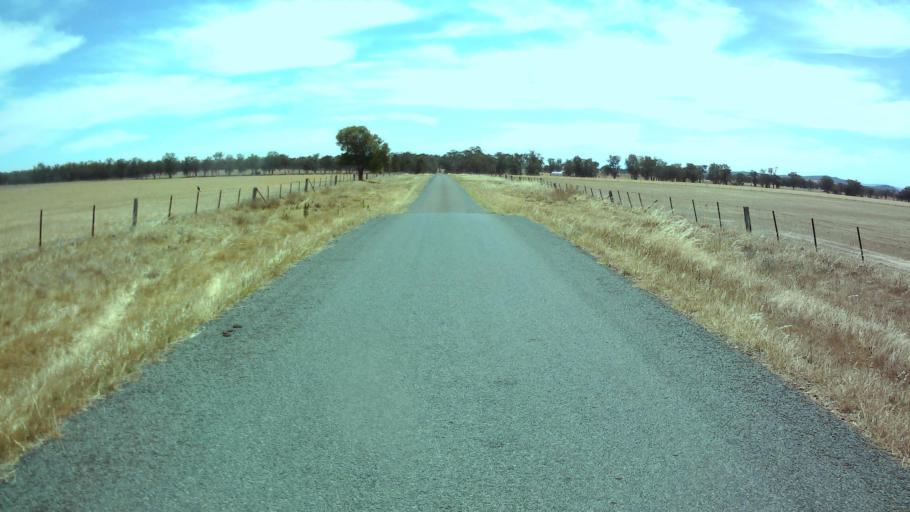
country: AU
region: New South Wales
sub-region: Weddin
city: Grenfell
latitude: -33.7464
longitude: 148.2076
